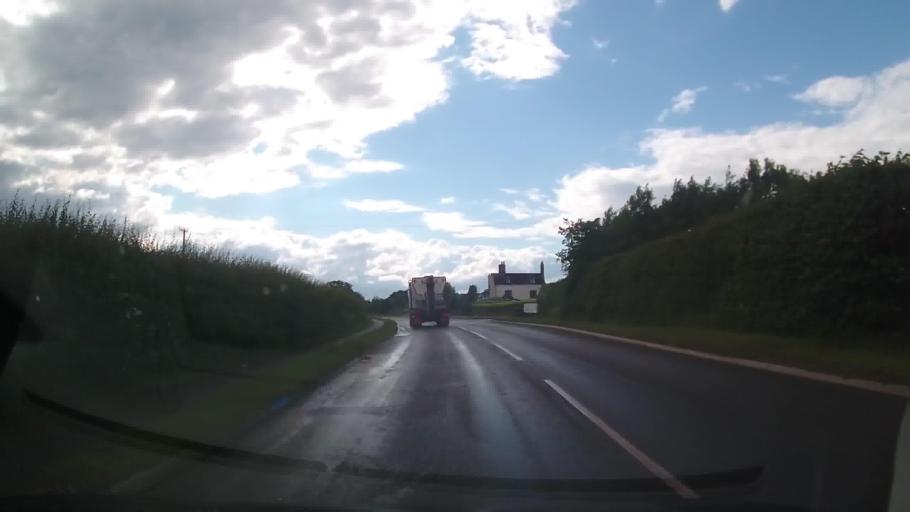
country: GB
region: England
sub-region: Telford and Wrekin
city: Ironbridge
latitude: 52.6616
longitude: -2.4945
